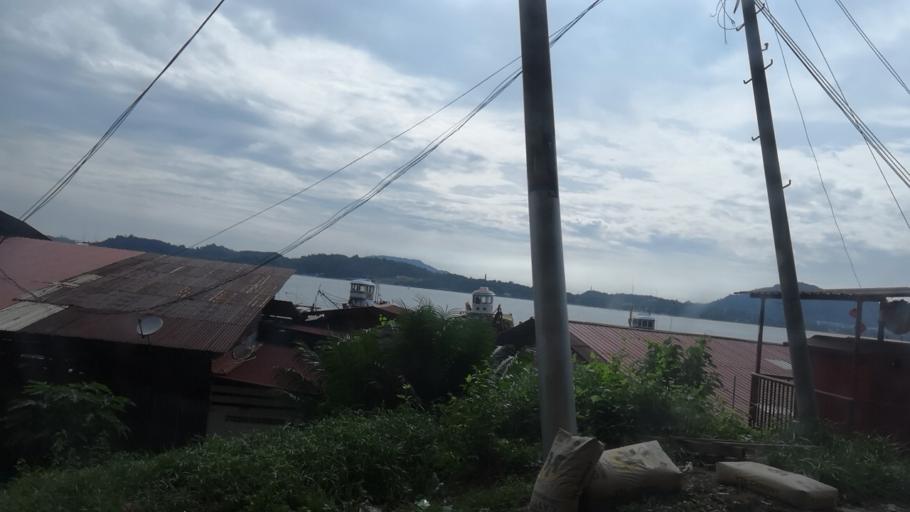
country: MY
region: Perak
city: Lumut
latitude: 4.2157
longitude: 100.5766
